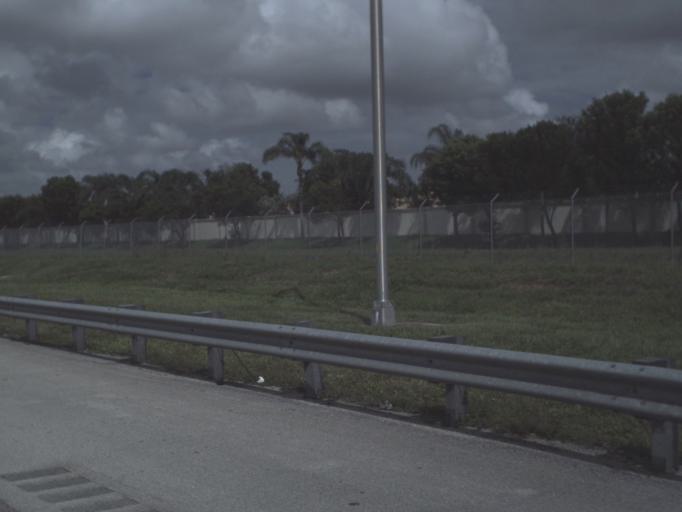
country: US
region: Florida
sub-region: Palm Beach County
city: Villages of Oriole
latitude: 26.5088
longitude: -80.1725
